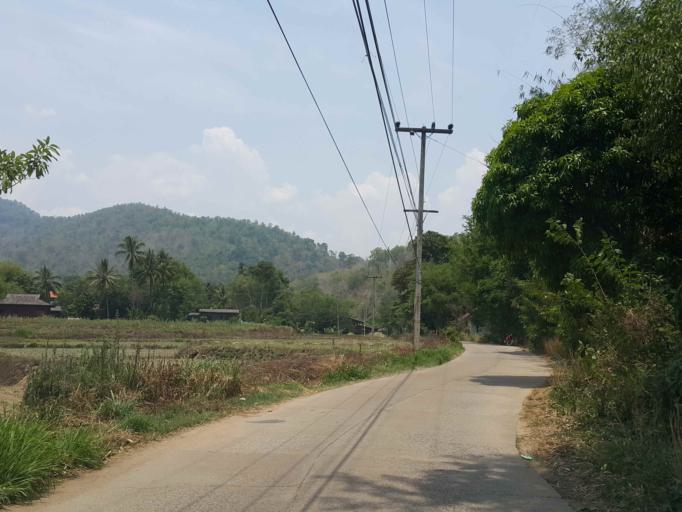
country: TH
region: Chiang Mai
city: Mae Taeng
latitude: 19.2197
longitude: 98.8495
